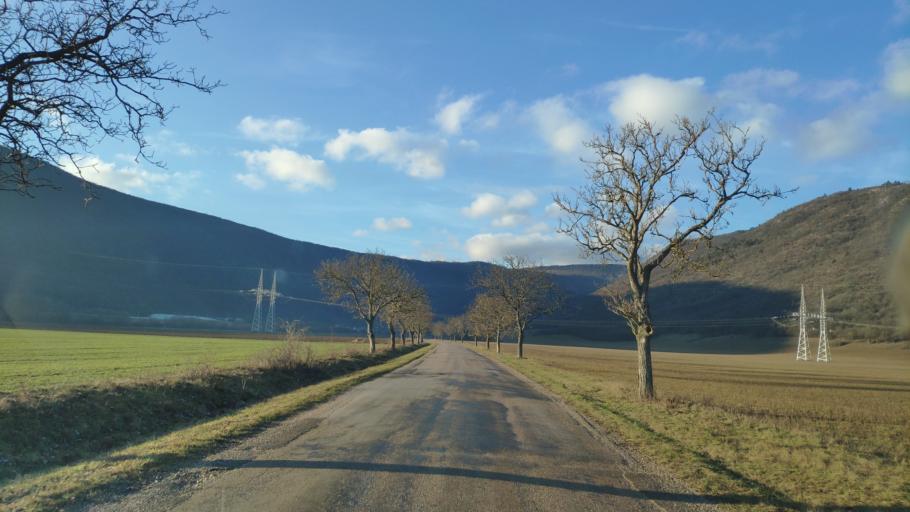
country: SK
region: Kosicky
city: Medzev
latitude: 48.6202
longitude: 20.8724
